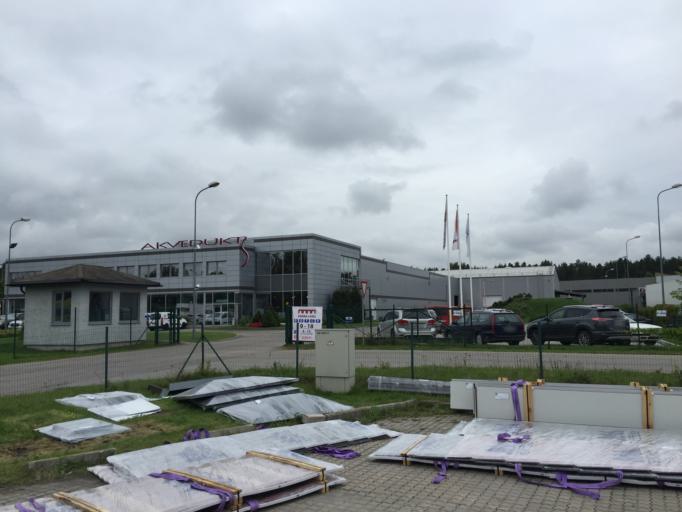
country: LV
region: Kekava
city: Balozi
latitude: 56.8897
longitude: 24.1456
